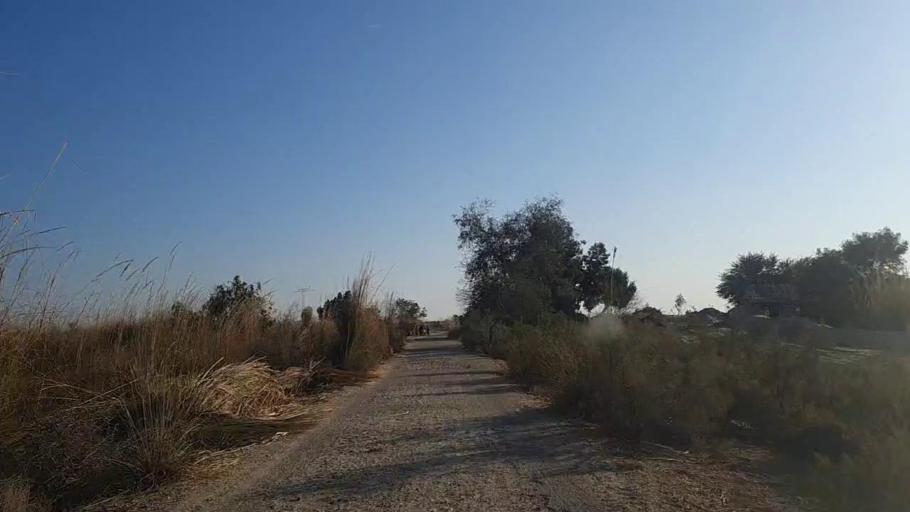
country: PK
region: Sindh
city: Khadro
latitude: 26.2751
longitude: 68.8603
